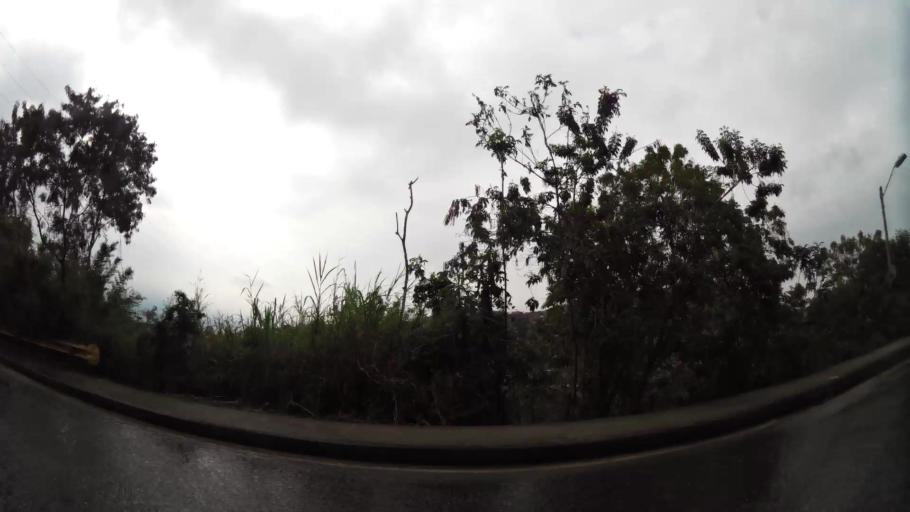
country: CO
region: Antioquia
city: Medellin
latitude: 6.2779
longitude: -75.6121
